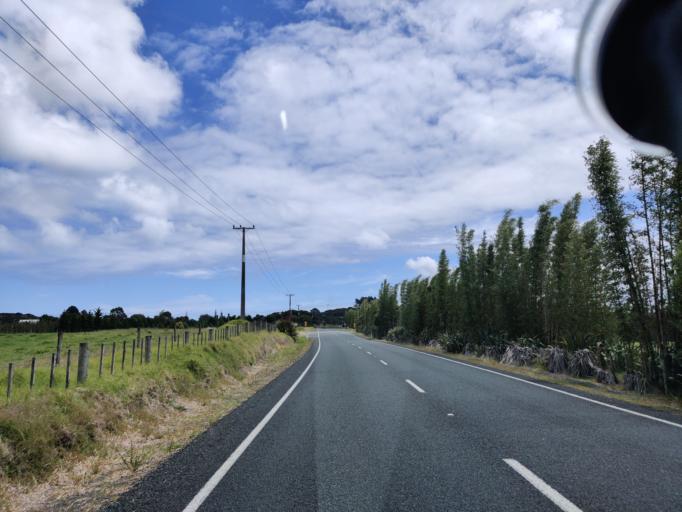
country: NZ
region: Northland
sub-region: Far North District
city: Kaitaia
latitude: -34.8725
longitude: 173.1507
